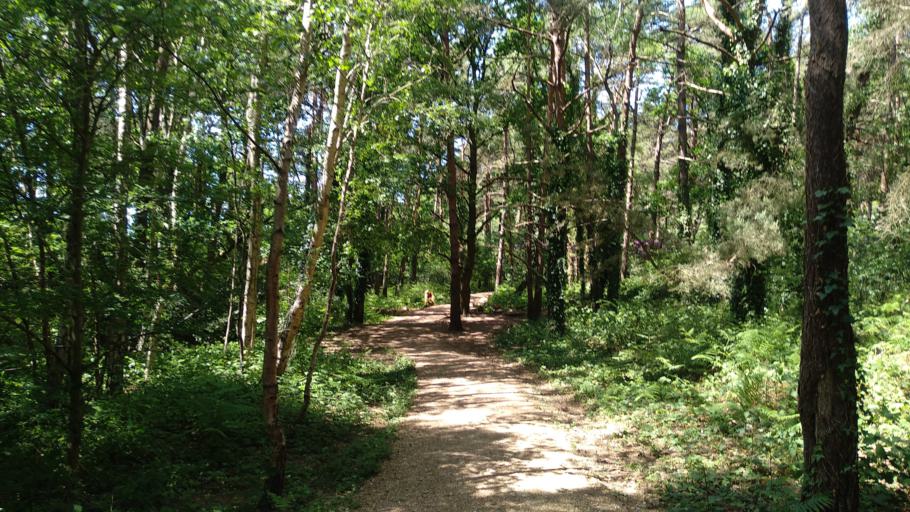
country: GB
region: England
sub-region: Dorset
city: Ferndown
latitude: 50.7854
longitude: -1.8947
